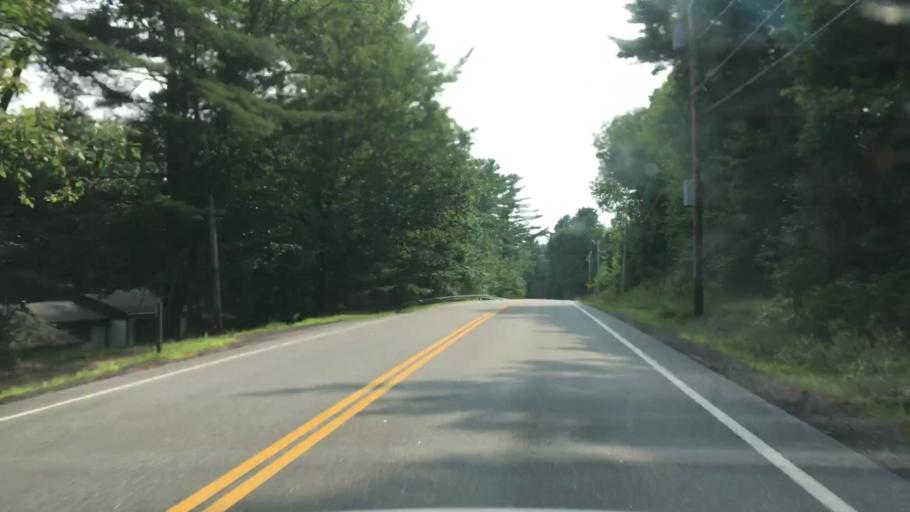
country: US
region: Maine
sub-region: Oxford County
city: South Paris
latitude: 44.2340
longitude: -70.4922
